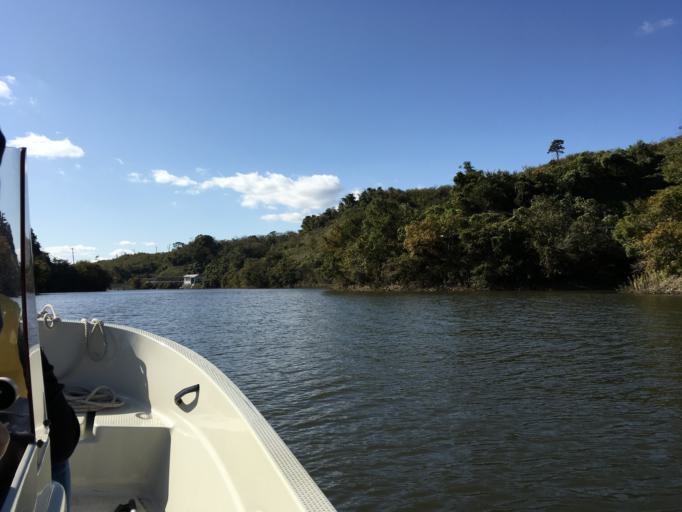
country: JP
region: Iwate
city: Ichinoseki
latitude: 38.7972
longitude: 141.2885
